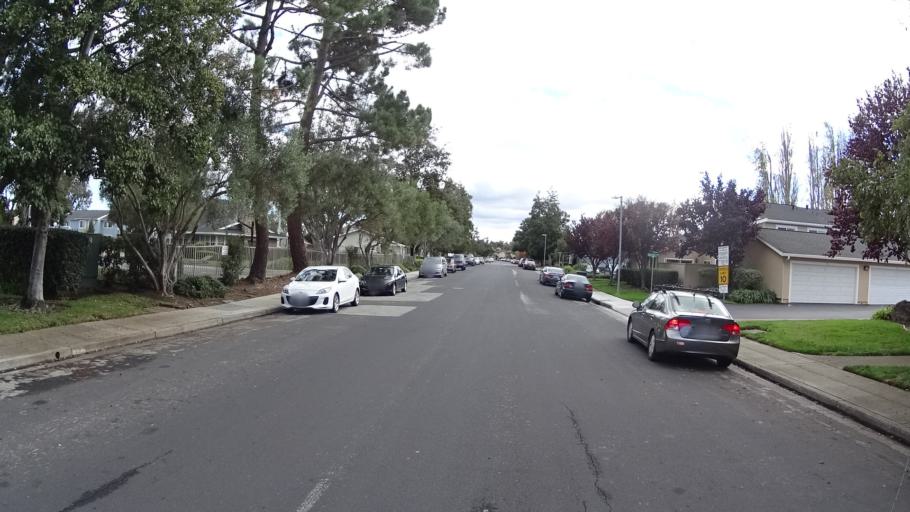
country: US
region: California
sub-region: San Mateo County
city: Foster City
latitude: 37.5604
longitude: -122.2640
